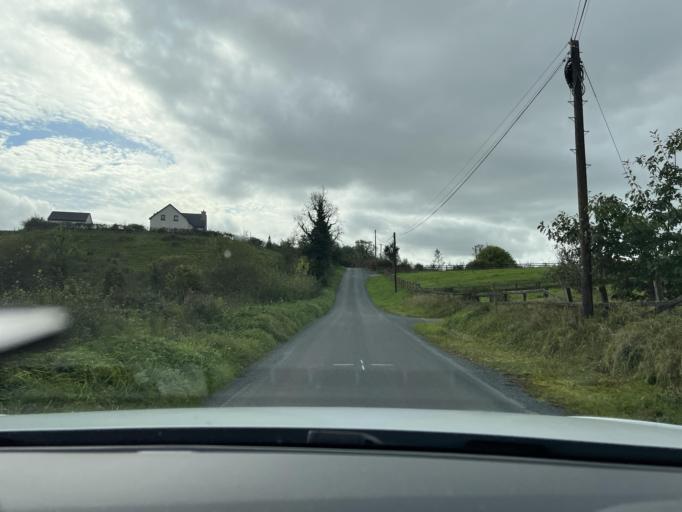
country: IE
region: Connaught
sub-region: County Leitrim
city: Carrick-on-Shannon
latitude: 53.9680
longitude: -8.0818
